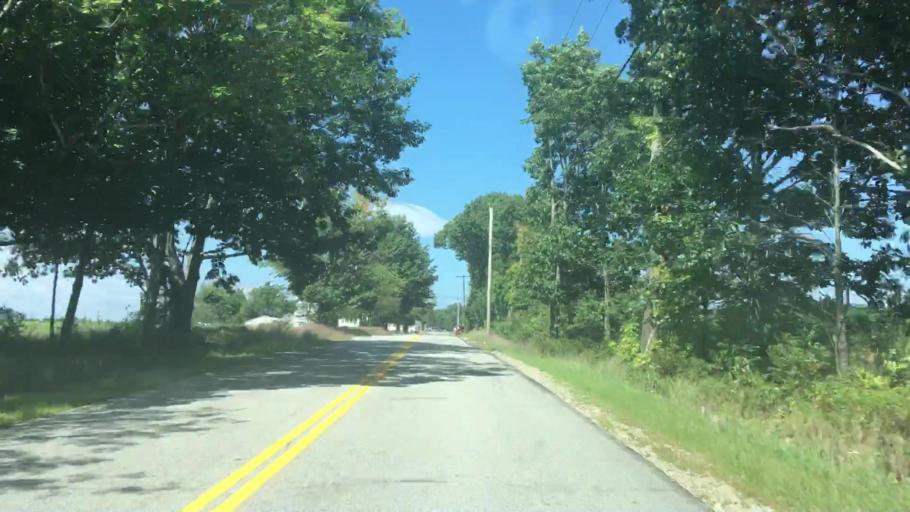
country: US
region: Maine
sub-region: Androscoggin County
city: Lisbon
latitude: 44.0524
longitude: -70.1148
